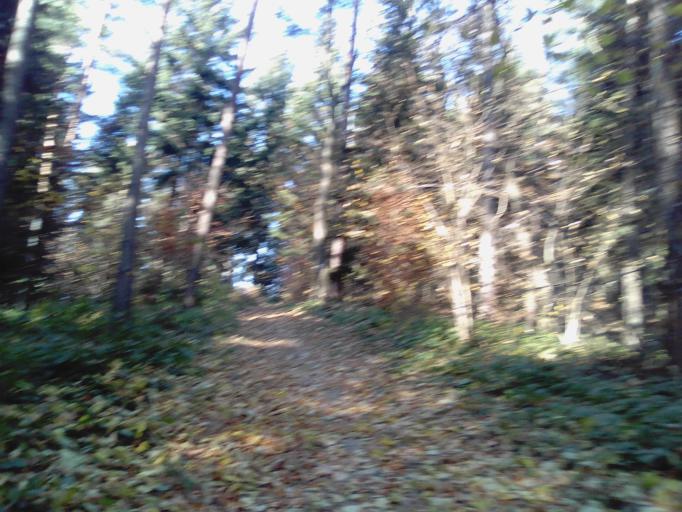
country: PL
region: Subcarpathian Voivodeship
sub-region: Powiat strzyzowski
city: Wysoka Strzyzowska
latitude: 49.8033
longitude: 21.7256
